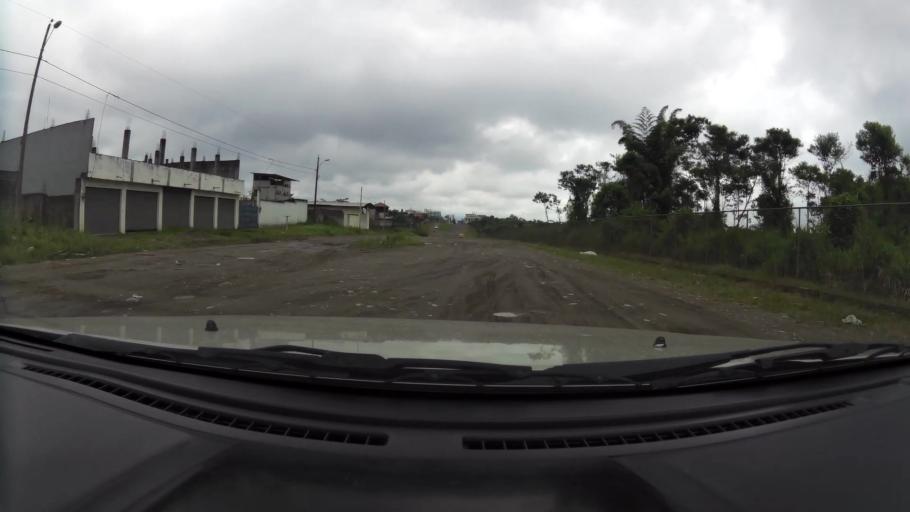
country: EC
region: Santo Domingo de los Tsachilas
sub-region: Canton Santo Domingo de los Colorados
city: Santo Domingo de los Colorados
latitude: -0.2411
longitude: -79.1603
